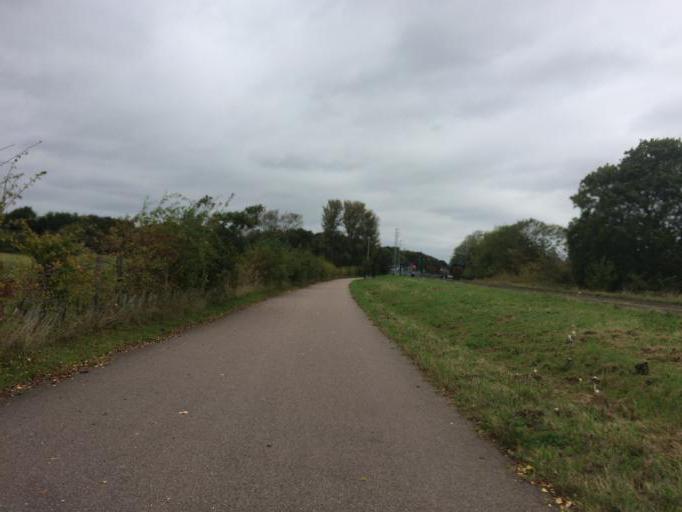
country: GB
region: England
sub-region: Cambridgeshire
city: Histon
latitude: 52.2640
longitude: 0.0779
